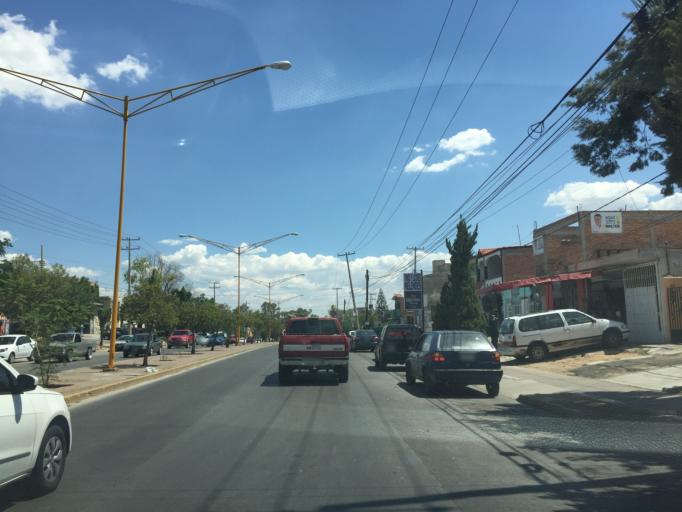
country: MX
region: Aguascalientes
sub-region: Aguascalientes
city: La Loma de los Negritos
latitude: 21.8492
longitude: -102.3193
